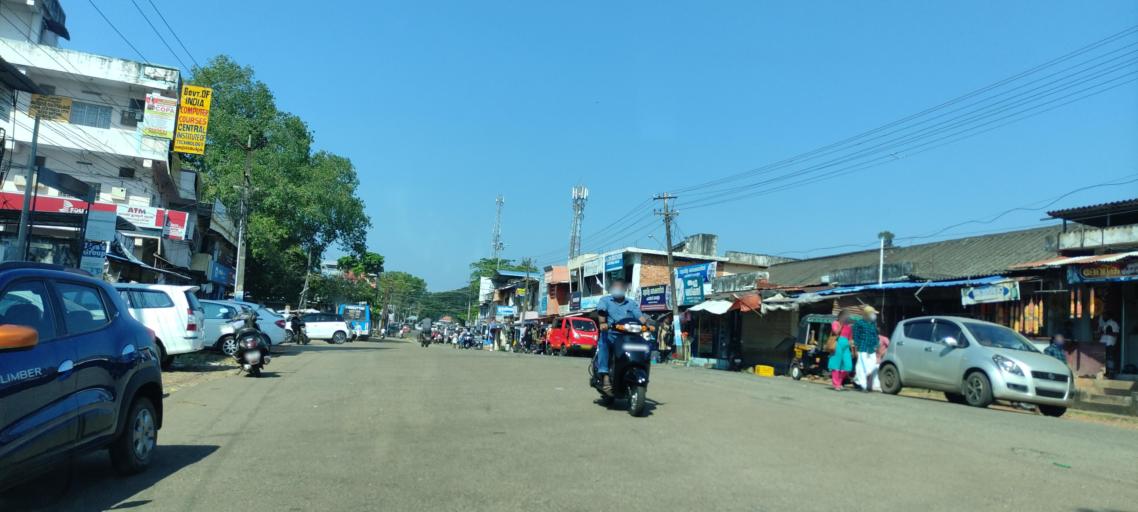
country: IN
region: Kerala
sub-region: Kollam
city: Panmana
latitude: 9.0425
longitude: 76.6274
